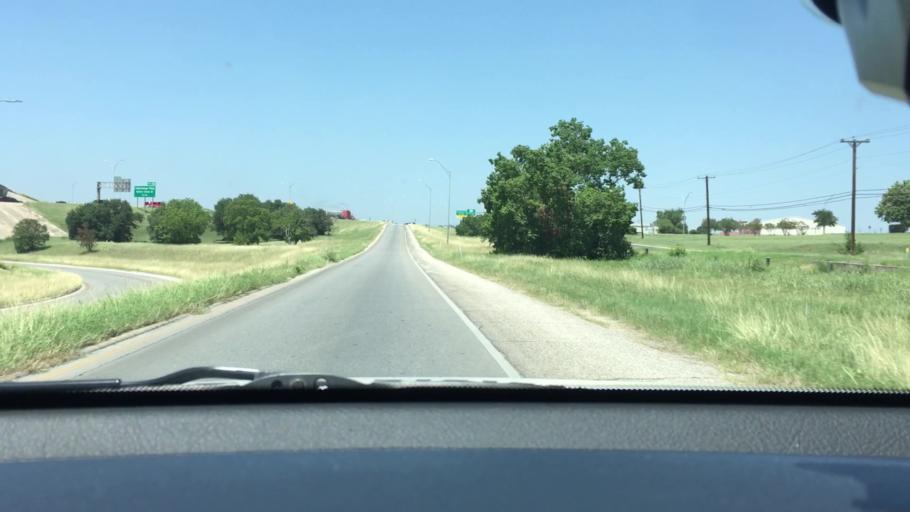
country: US
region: Texas
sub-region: Bexar County
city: Windcrest
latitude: 29.5146
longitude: -98.4029
